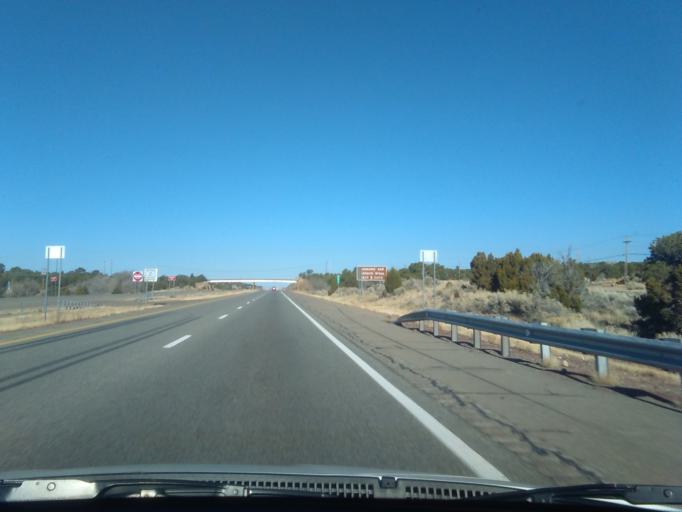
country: US
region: New Mexico
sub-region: Santa Fe County
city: Eldorado at Santa Fe
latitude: 35.5979
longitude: -105.9074
